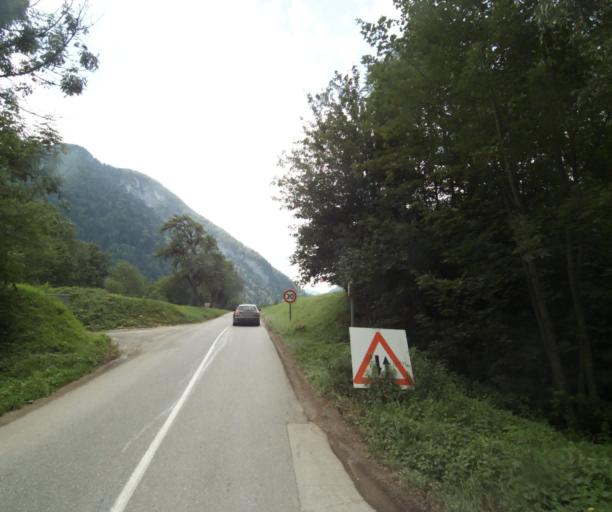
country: FR
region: Rhone-Alpes
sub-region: Departement de la Haute-Savoie
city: Thones
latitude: 45.8965
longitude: 6.3066
